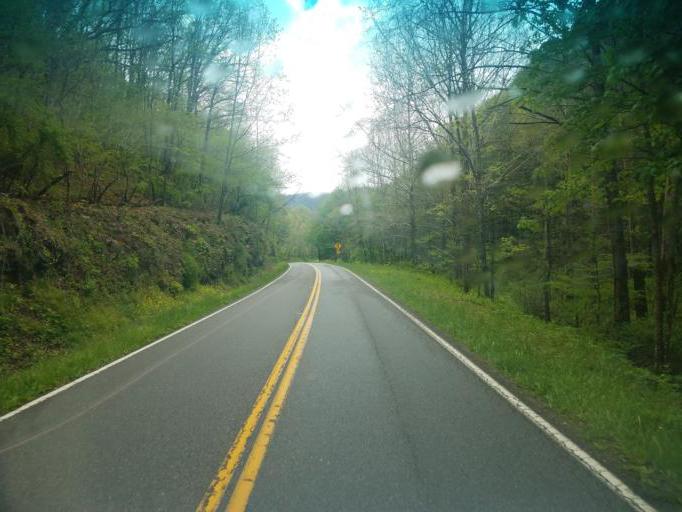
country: US
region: Virginia
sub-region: Smyth County
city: Marion
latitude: 36.9411
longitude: -81.5292
